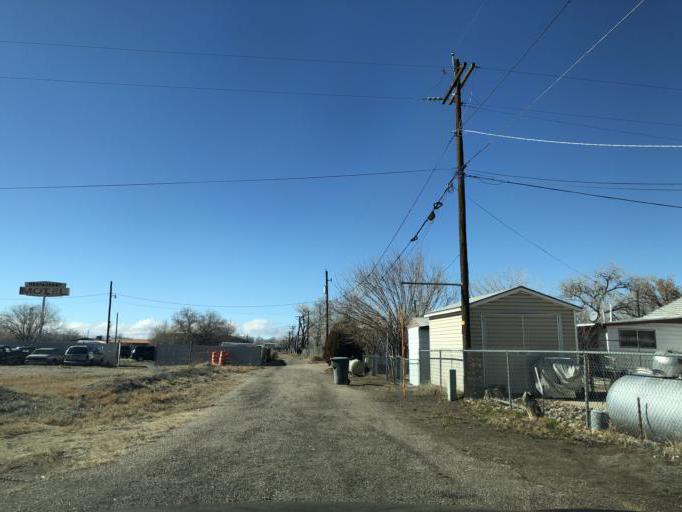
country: US
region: Utah
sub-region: Carbon County
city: East Carbon City
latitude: 38.9963
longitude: -110.1507
